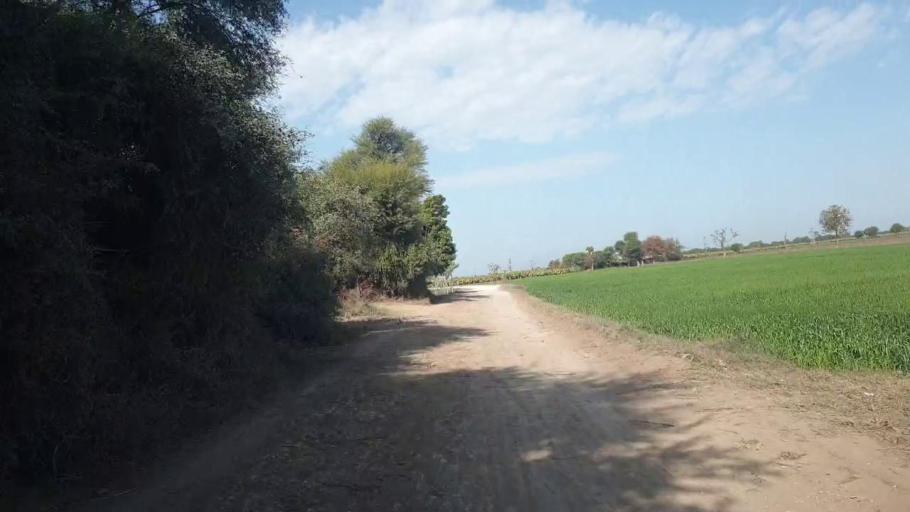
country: PK
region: Sindh
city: Sakrand
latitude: 25.9774
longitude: 68.3390
